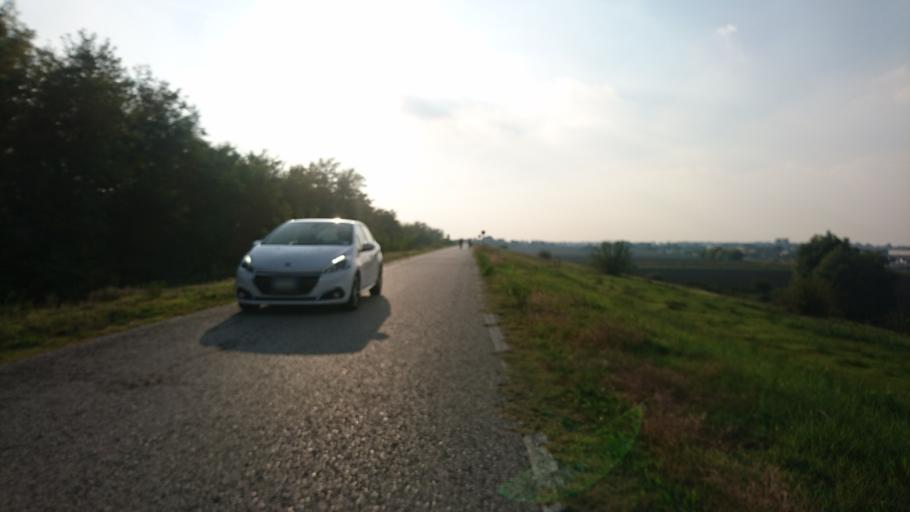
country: IT
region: Veneto
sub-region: Provincia di Rovigo
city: Canaro
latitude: 44.9260
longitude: 11.7045
